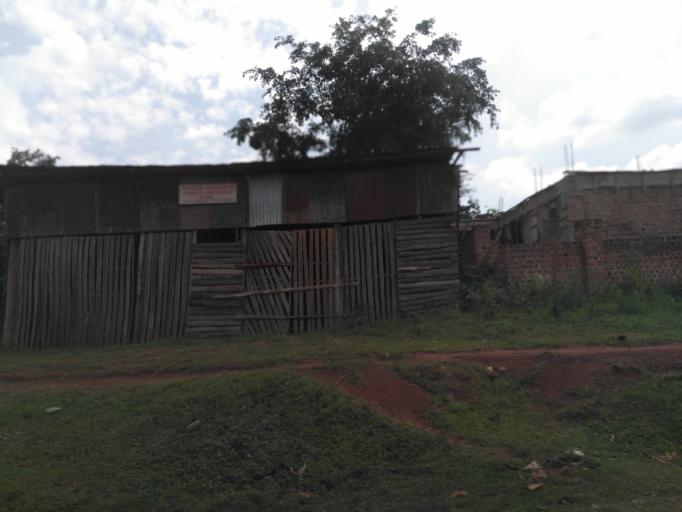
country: UG
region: Central Region
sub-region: Wakiso District
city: Kireka
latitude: 0.4618
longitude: 32.6057
